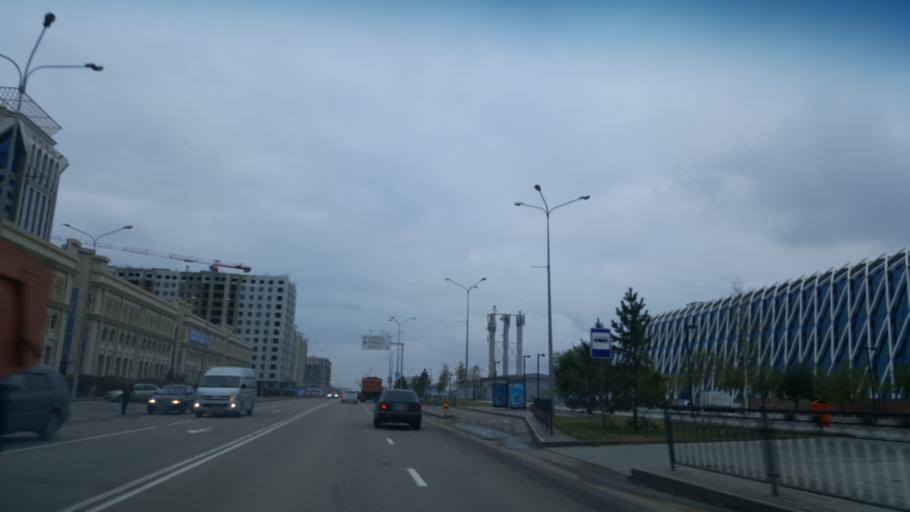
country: KZ
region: Astana Qalasy
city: Astana
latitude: 51.1214
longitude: 71.4742
